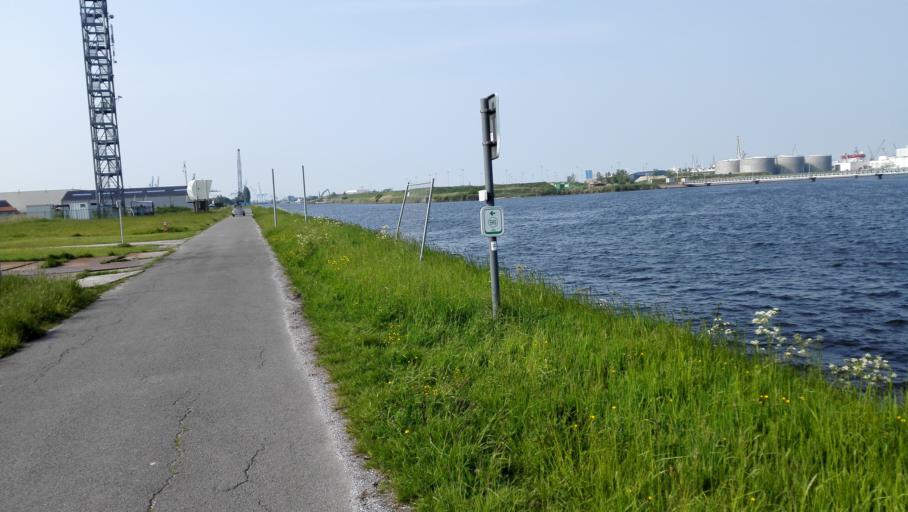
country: BE
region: Flanders
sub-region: Provincie West-Vlaanderen
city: Zeebrugge
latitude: 51.3092
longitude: 3.2023
